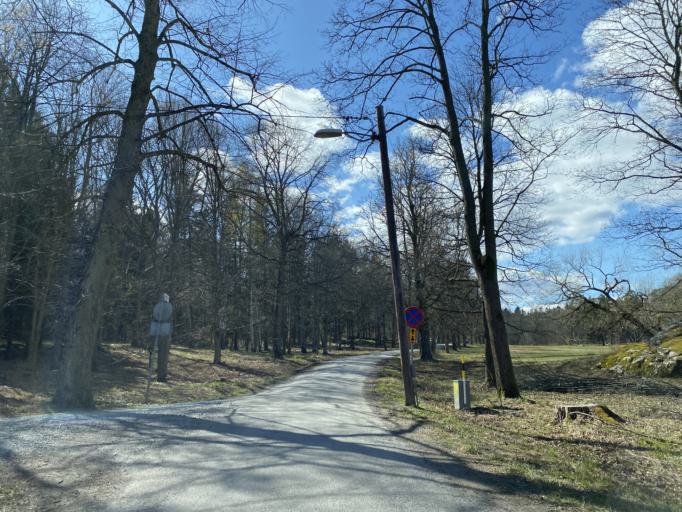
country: SE
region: Stockholm
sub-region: Lidingo
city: Lidingoe
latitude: 59.3370
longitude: 18.1410
